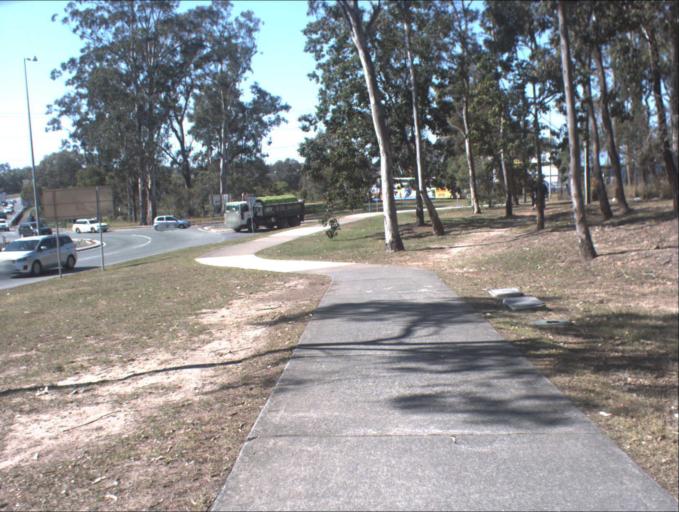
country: AU
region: Queensland
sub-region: Logan
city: Logan City
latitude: -27.6639
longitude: 153.1187
